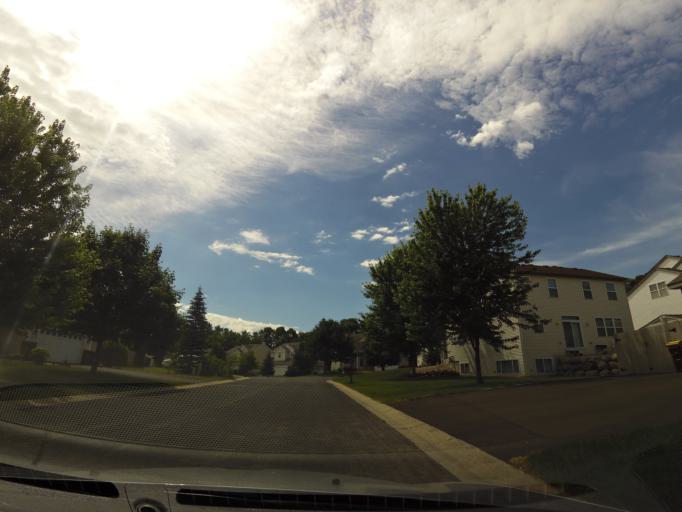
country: US
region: Minnesota
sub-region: Scott County
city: Prior Lake
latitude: 44.7406
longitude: -93.4725
